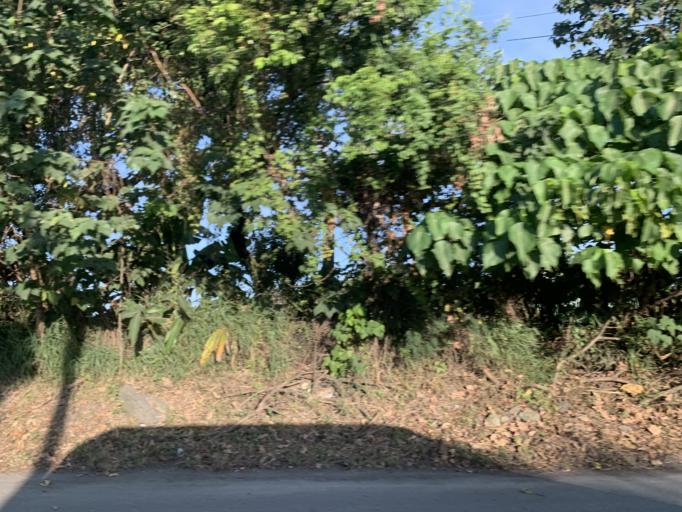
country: TW
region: Taiwan
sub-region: Hualien
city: Hualian
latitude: 24.0079
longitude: 121.6316
